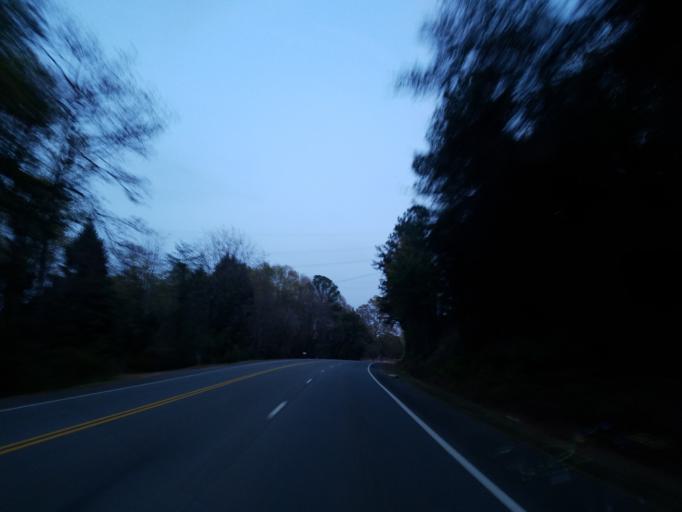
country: US
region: Georgia
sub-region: Pickens County
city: Jasper
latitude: 34.4925
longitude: -84.4647
